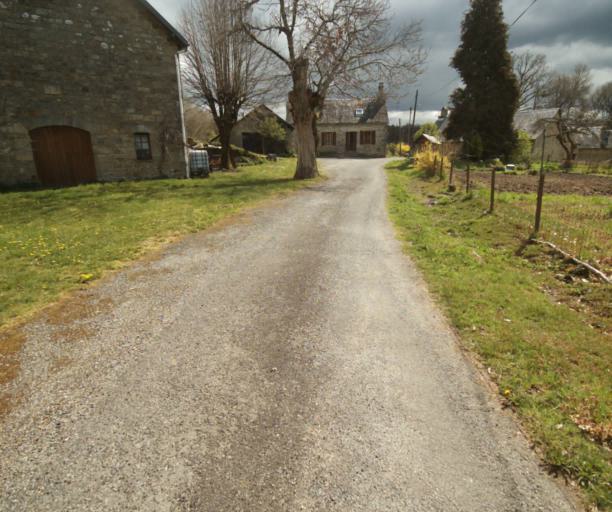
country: FR
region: Limousin
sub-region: Departement de la Correze
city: Correze
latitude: 45.2737
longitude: 1.8957
